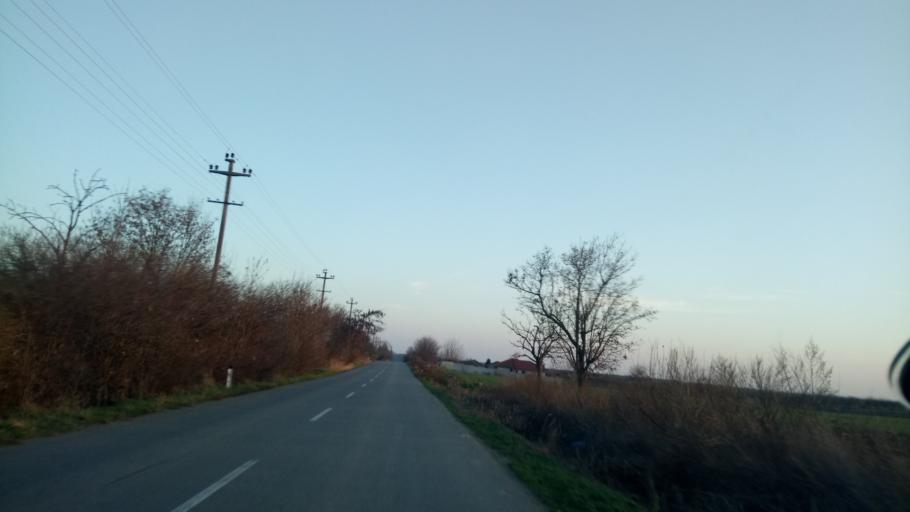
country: RS
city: Surduk
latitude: 45.0962
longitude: 20.2938
